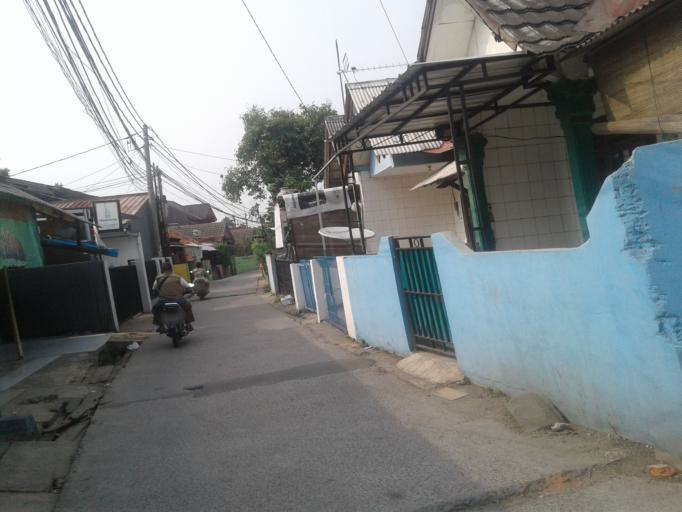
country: ID
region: West Java
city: Depok
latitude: -6.3738
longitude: 106.8376
